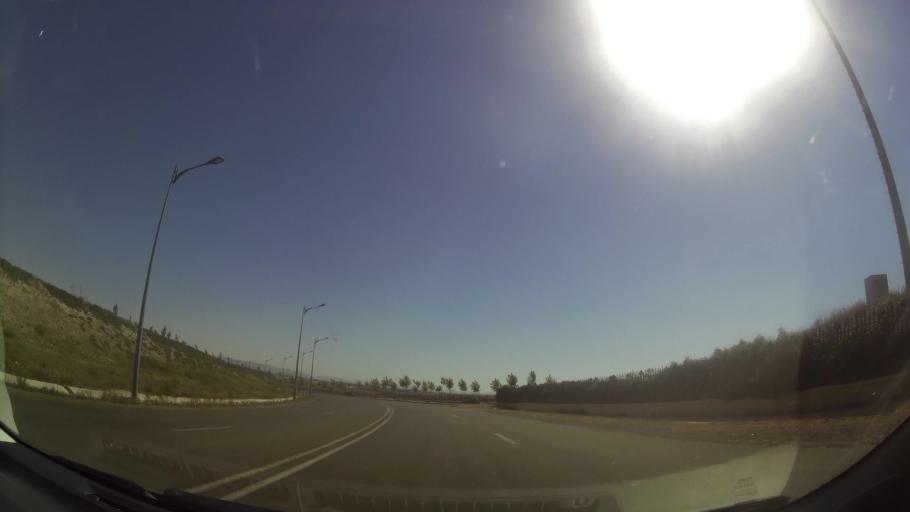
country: MA
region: Oriental
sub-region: Oujda-Angad
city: Oujda
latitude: 34.7399
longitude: -1.9181
